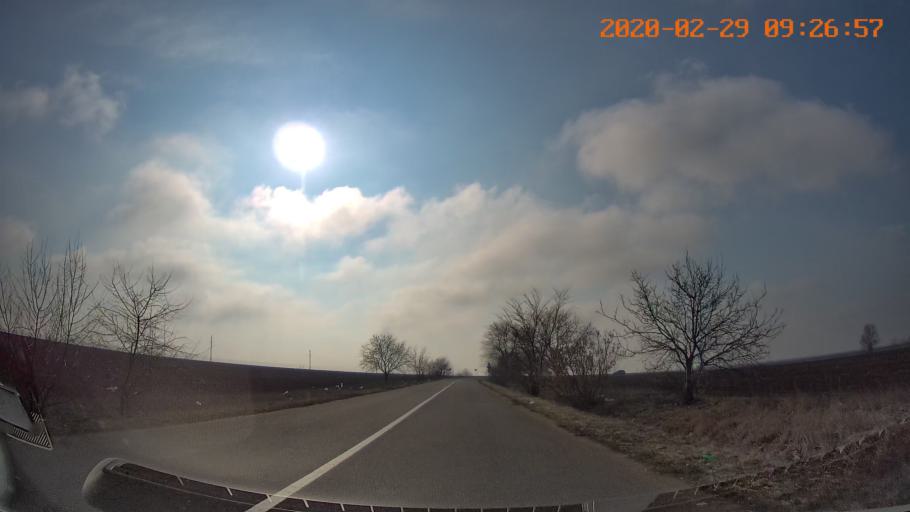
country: MD
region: Telenesti
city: Pervomaisc
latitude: 46.7007
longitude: 29.9457
